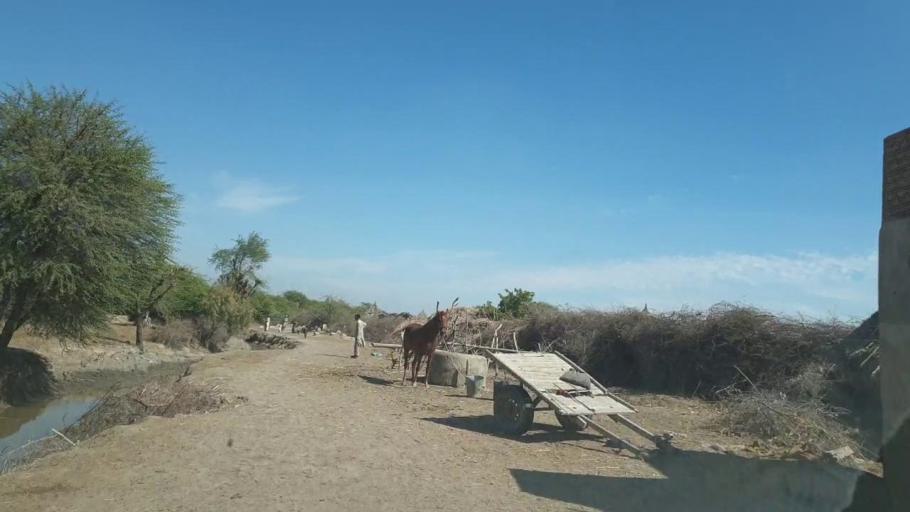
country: PK
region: Sindh
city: Pithoro
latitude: 25.6068
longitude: 69.2886
